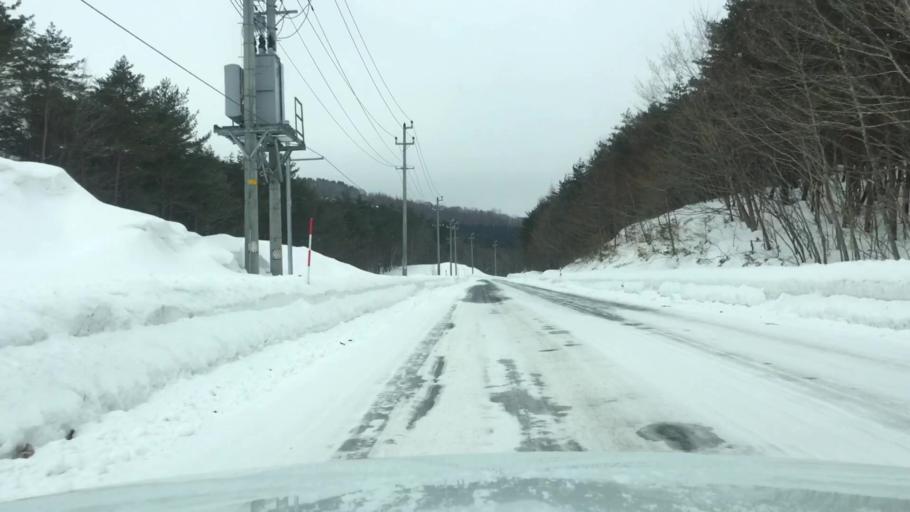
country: JP
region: Iwate
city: Shizukuishi
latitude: 39.9735
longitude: 141.0024
